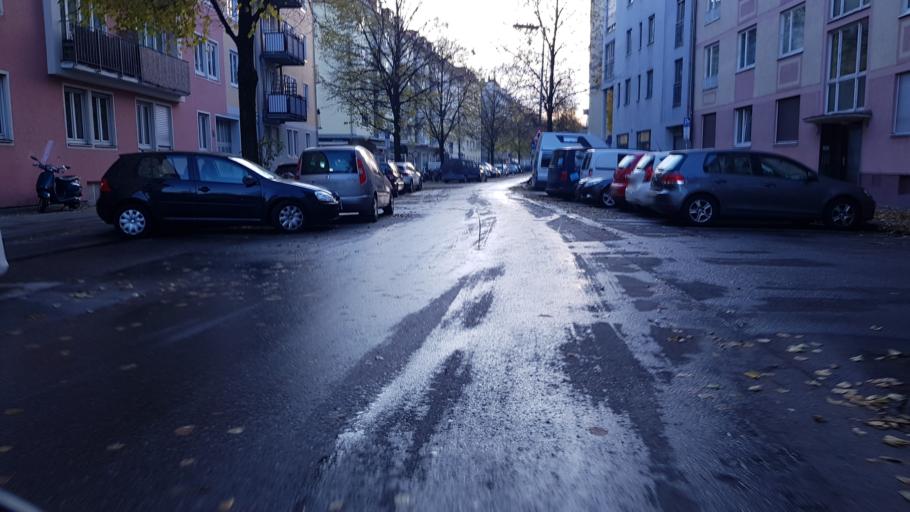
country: DE
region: Bavaria
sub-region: Upper Bavaria
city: Munich
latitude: 48.1202
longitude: 11.5712
